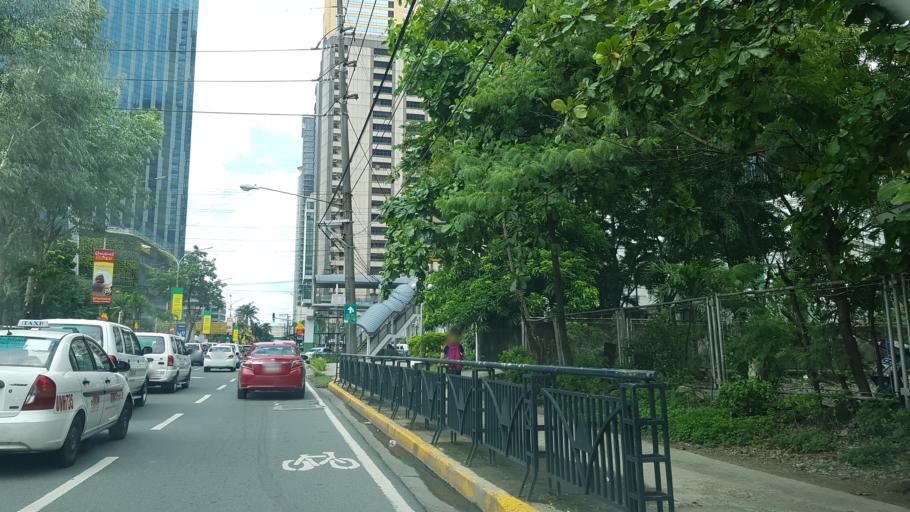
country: PH
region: Metro Manila
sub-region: Pasig
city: Pasig City
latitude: 14.5834
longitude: 121.0601
